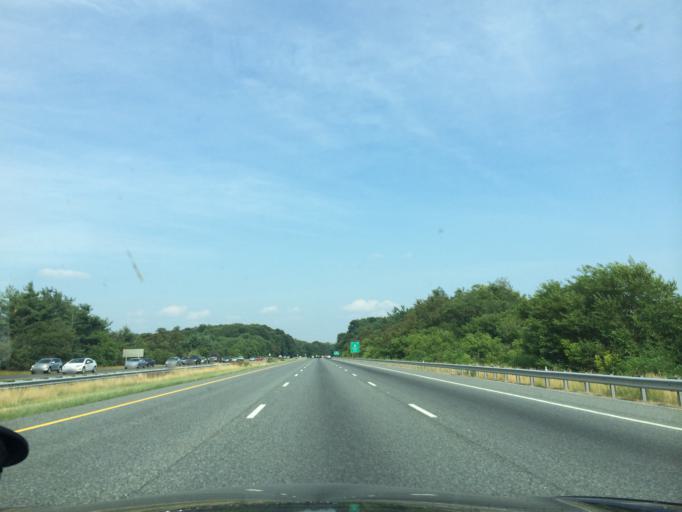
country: US
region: Maryland
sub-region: Carroll County
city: Mount Airy
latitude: 39.3471
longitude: -77.0904
